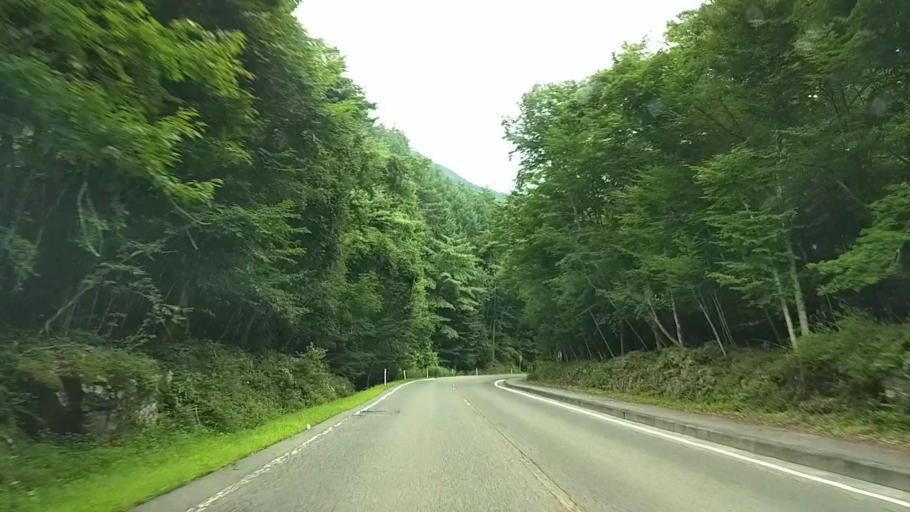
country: JP
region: Yamanashi
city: Fujikawaguchiko
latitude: 35.4957
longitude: 138.6494
